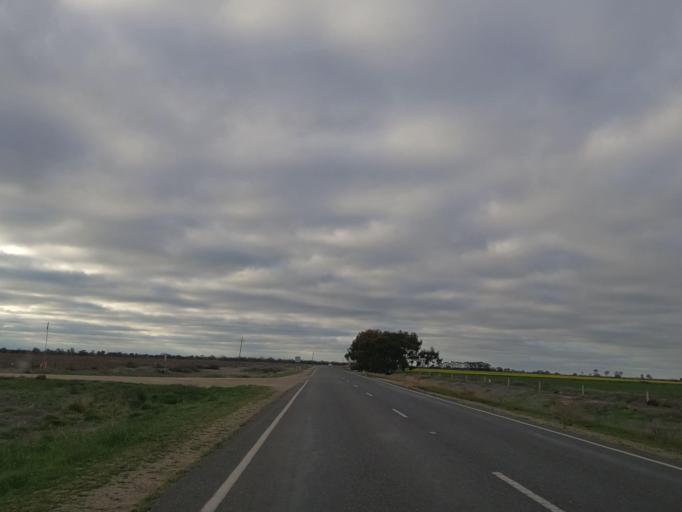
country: AU
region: Victoria
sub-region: Swan Hill
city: Swan Hill
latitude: -35.8316
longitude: 143.9439
